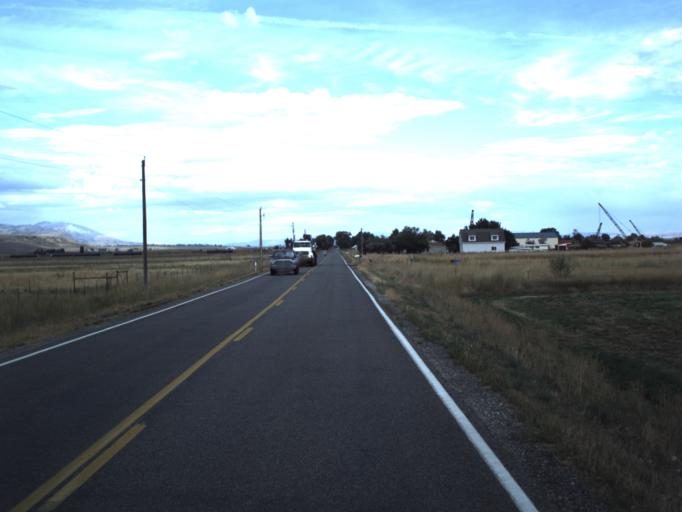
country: US
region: Utah
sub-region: Cache County
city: Lewiston
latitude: 41.9511
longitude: -111.9539
